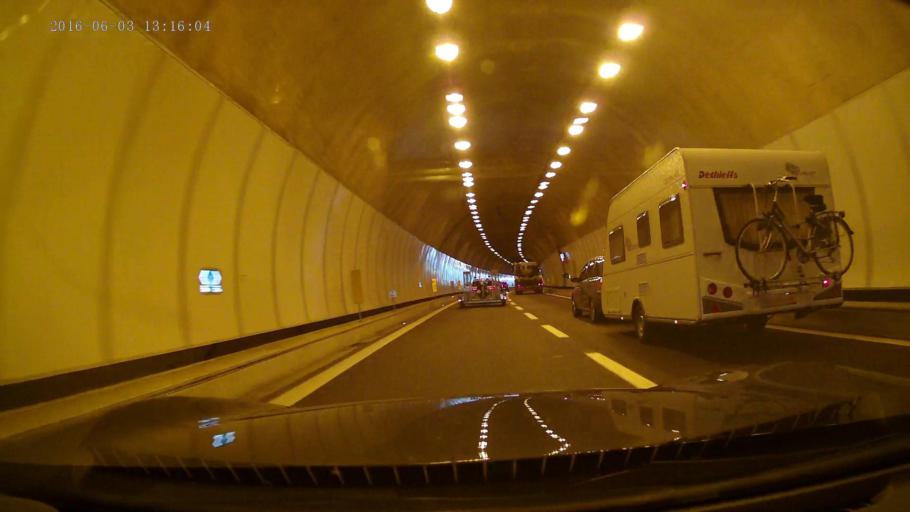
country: IT
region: Trentino-Alto Adige
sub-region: Bolzano
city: Ponte Gardena
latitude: 46.5958
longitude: 11.5327
